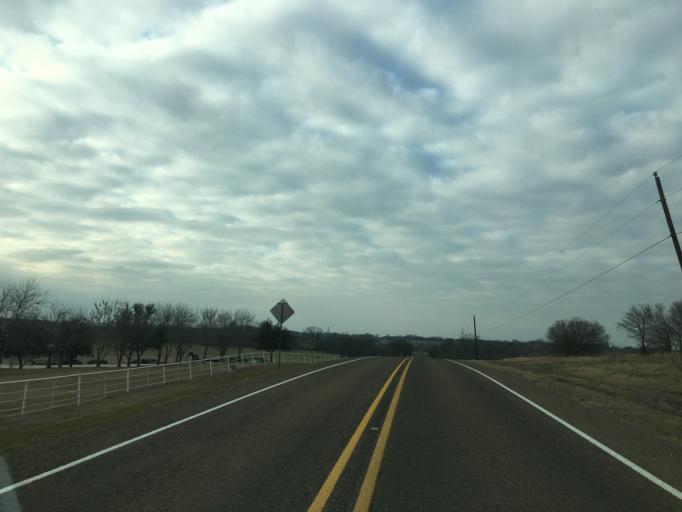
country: US
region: Texas
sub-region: Ellis County
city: Palmer
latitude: 32.4345
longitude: -96.6868
